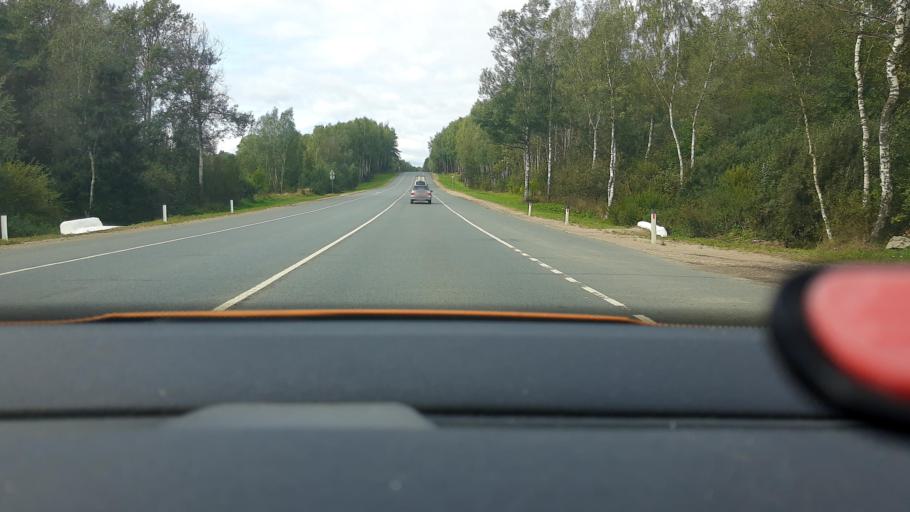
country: RU
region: Moskovskaya
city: Lesnoy
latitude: 56.0798
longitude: 38.0202
